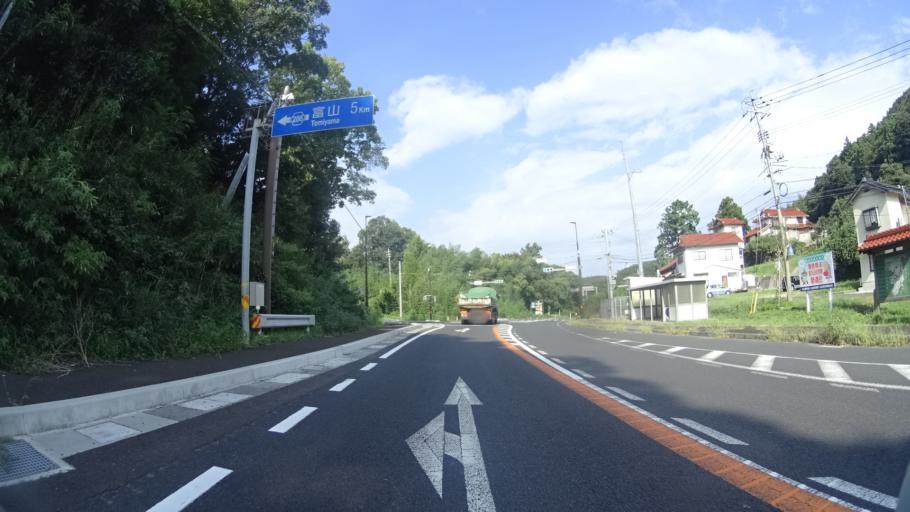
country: JP
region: Shimane
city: Odacho-oda
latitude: 35.2485
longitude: 132.5667
